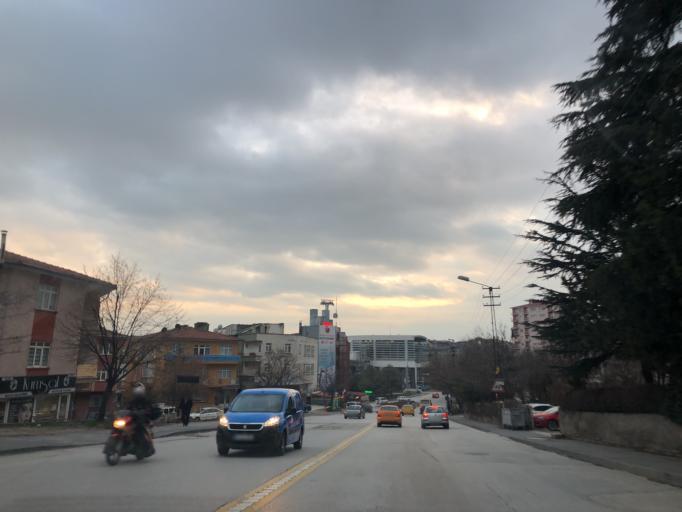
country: TR
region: Ankara
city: Ankara
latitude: 39.9713
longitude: 32.8100
